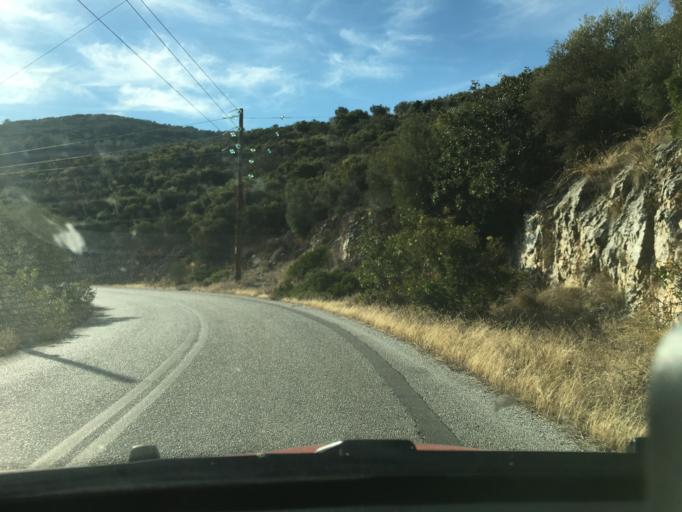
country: GR
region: Central Macedonia
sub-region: Nomos Chalkidikis
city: Agios Nikolaos
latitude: 40.3277
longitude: 23.7024
